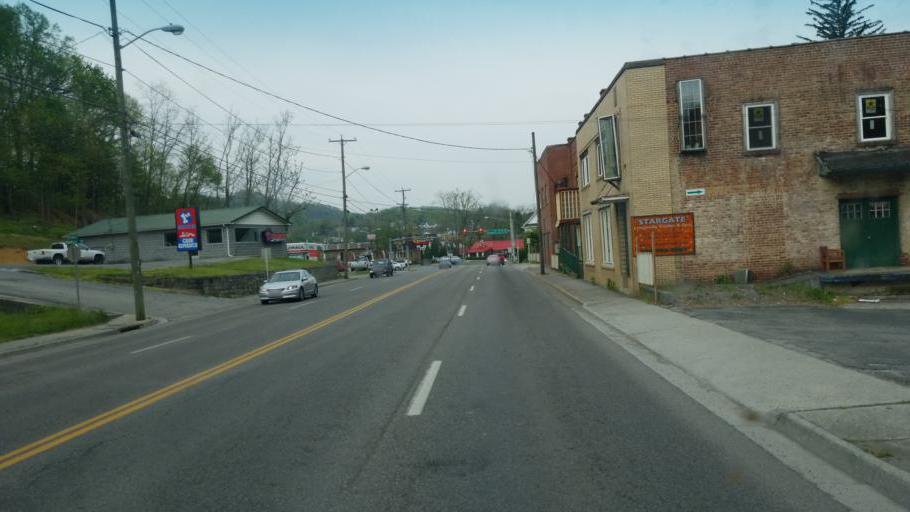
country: US
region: Virginia
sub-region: Smyth County
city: Marion
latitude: 36.8378
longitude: -81.5151
